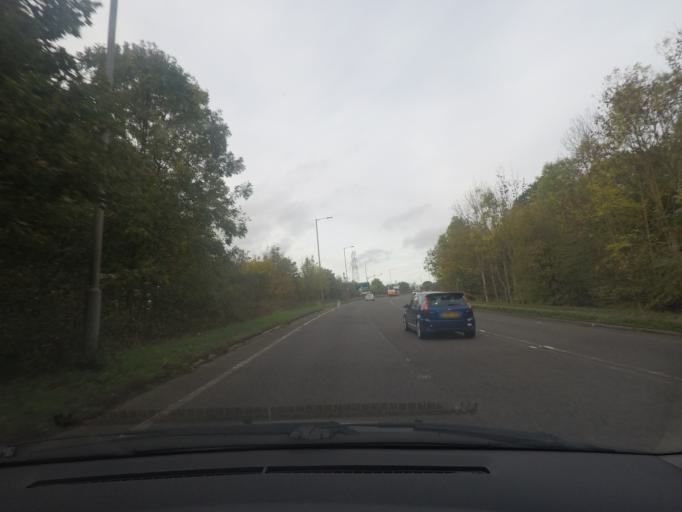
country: GB
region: England
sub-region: Sheffield
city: Chapletown
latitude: 53.4843
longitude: -1.4954
